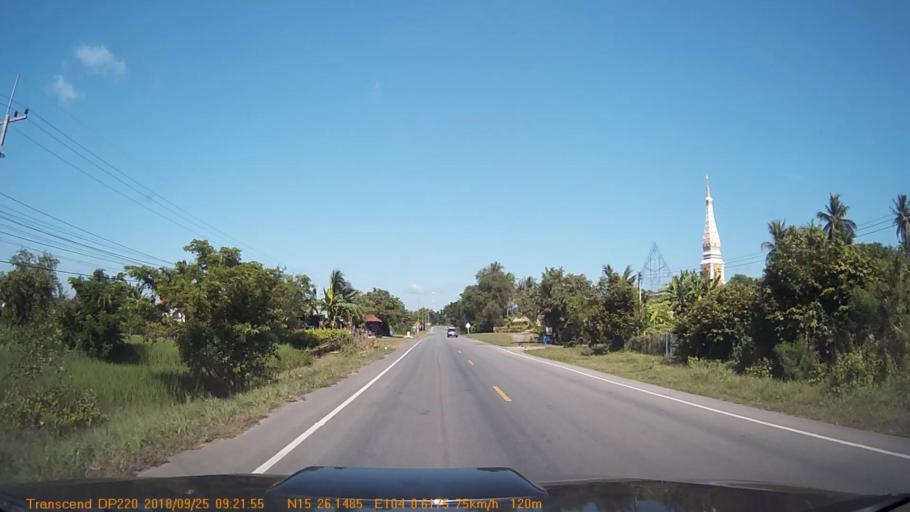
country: TH
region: Roi Et
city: Phon Sai
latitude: 15.4358
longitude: 104.0104
